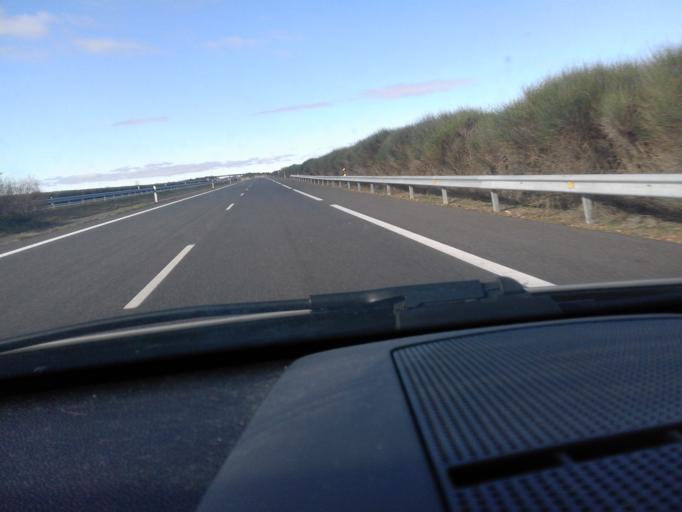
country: ES
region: Castille and Leon
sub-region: Provincia de Palencia
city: Bustillo del Paramo de Carrion
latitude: 42.3477
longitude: -4.7155
